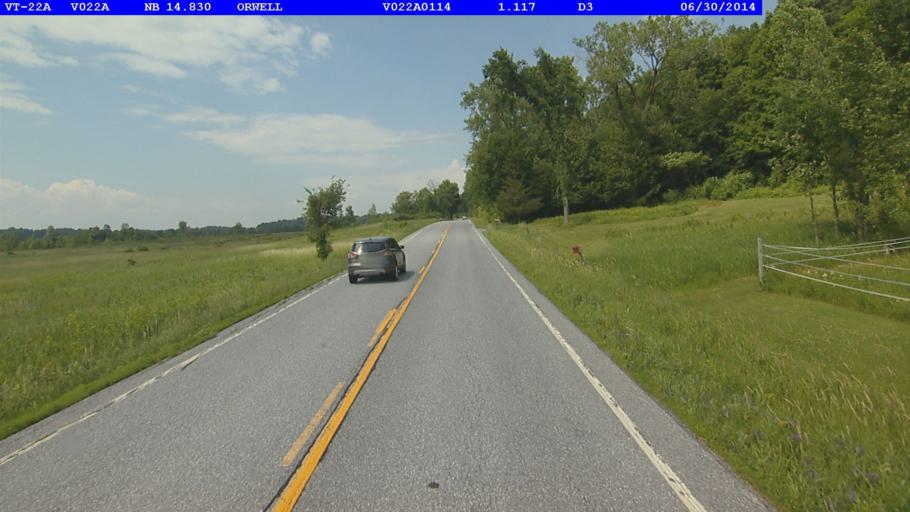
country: US
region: New York
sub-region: Essex County
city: Ticonderoga
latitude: 43.7731
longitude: -73.3087
